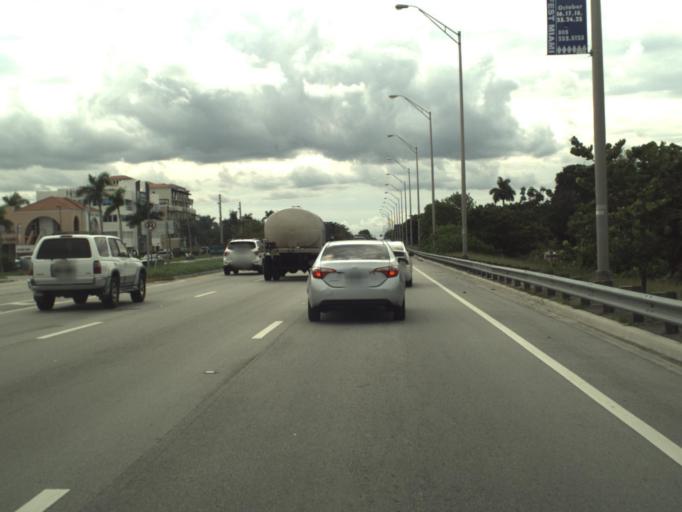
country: US
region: Florida
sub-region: Miami-Dade County
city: Westchester
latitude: 25.7623
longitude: -80.3297
